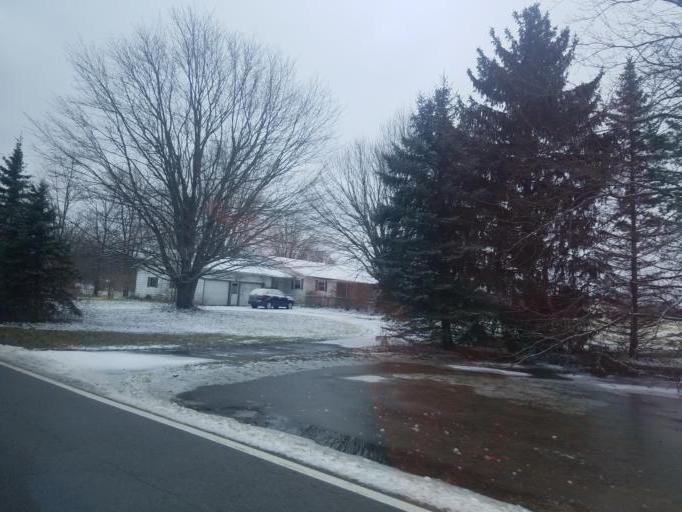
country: US
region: Ohio
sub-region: Licking County
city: Johnstown
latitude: 40.1034
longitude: -82.7078
